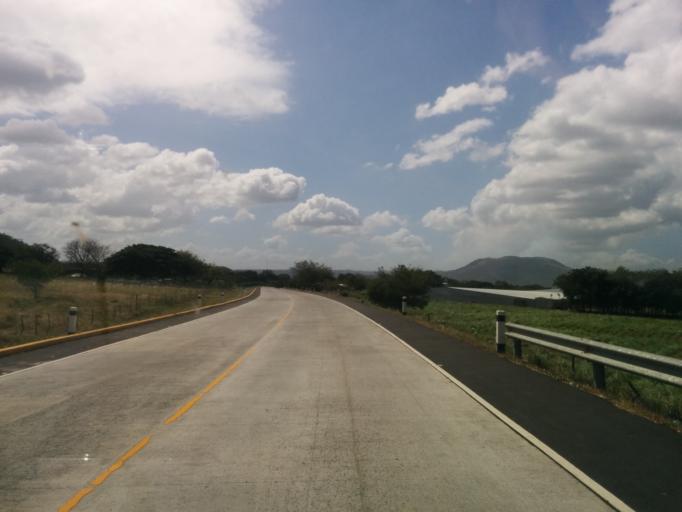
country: NI
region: Masaya
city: Nindiri
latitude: 12.0024
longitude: -86.0992
